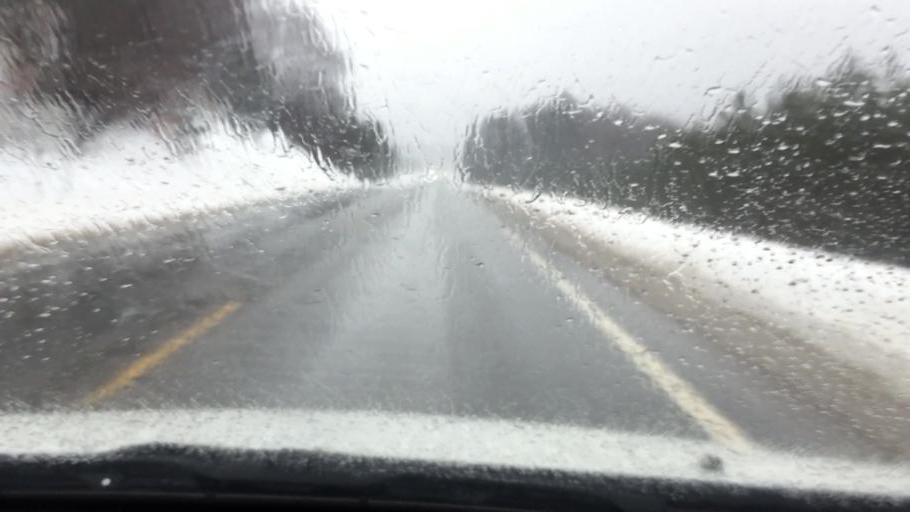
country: US
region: Michigan
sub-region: Antrim County
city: Mancelona
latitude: 44.9671
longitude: -85.0537
